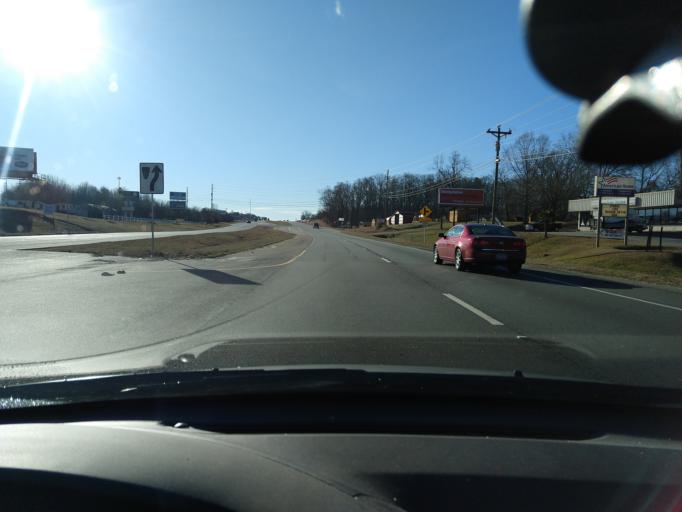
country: US
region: Georgia
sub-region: Jackson County
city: Commerce
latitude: 34.2424
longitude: -83.4576
